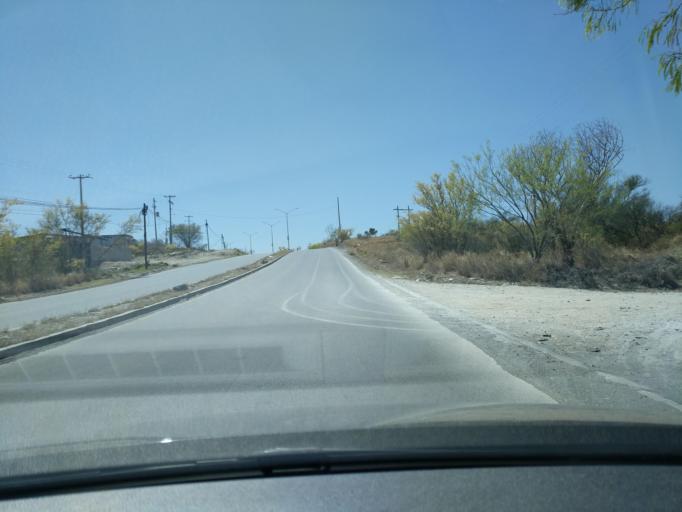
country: MX
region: Nuevo Leon
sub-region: Apodaca
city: Artemio Trevino
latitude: 25.8081
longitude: -100.1554
